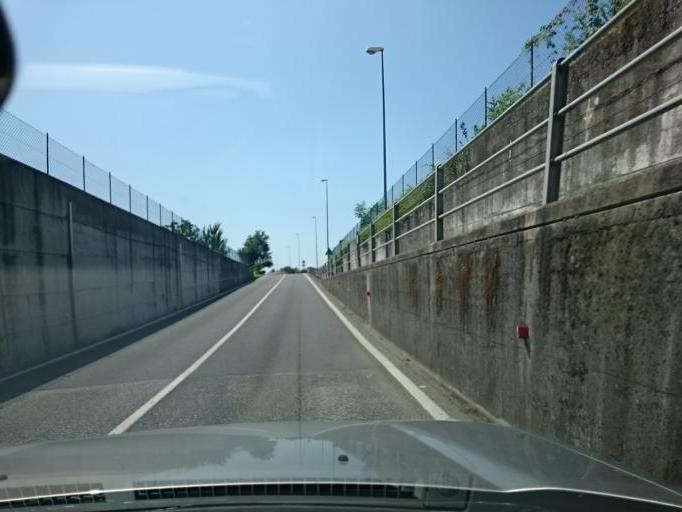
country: IT
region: Veneto
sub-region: Provincia di Padova
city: Villaguattera
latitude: 45.4409
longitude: 11.8220
